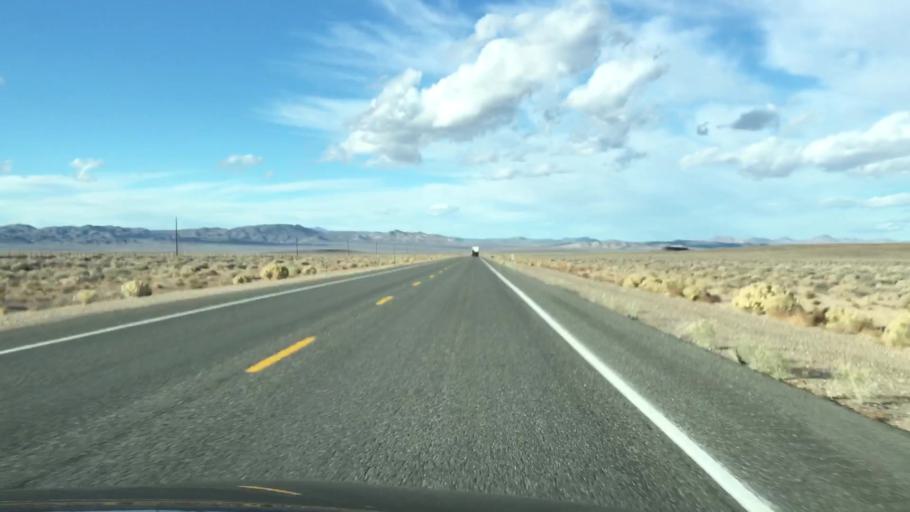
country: US
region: Nevada
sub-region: Esmeralda County
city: Goldfield
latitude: 37.4118
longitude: -117.1531
